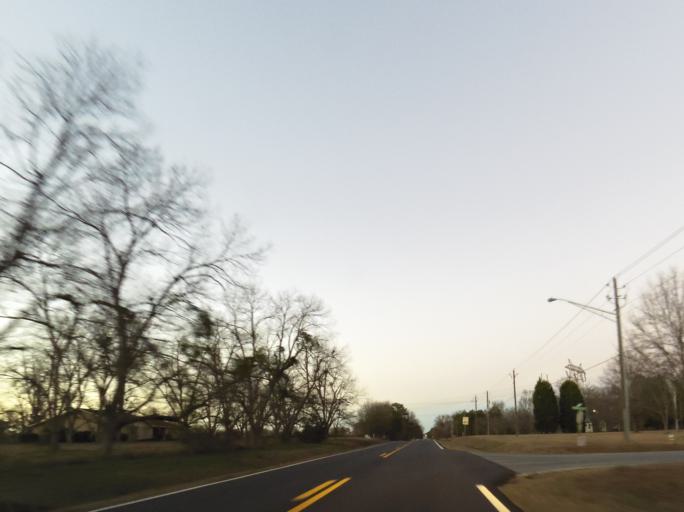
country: US
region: Georgia
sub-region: Peach County
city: Byron
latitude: 32.6339
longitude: -83.7573
